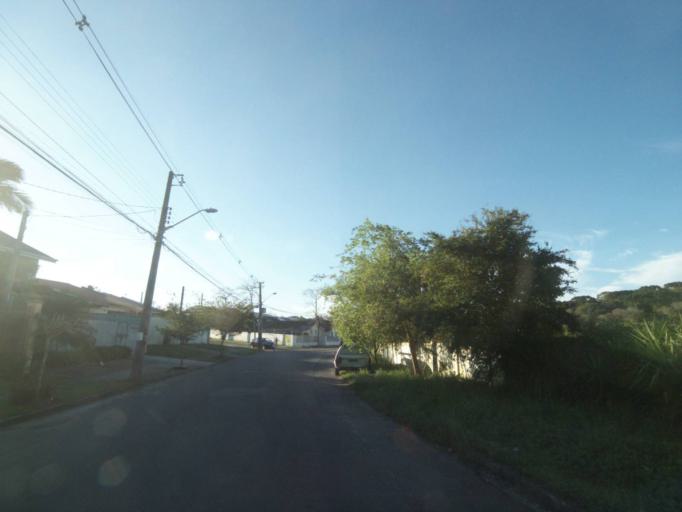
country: BR
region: Parana
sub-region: Curitiba
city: Curitiba
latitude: -25.3751
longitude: -49.2502
